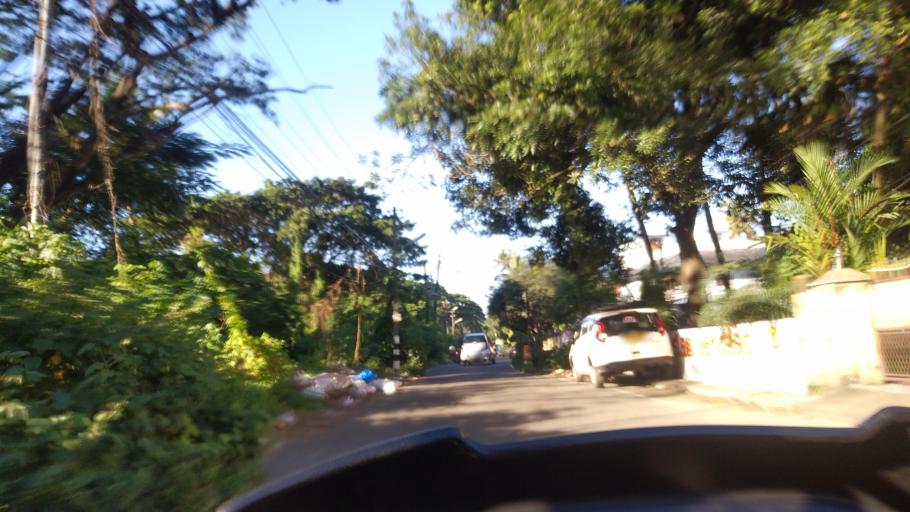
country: IN
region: Kerala
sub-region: Ernakulam
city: Cochin
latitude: 9.9978
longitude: 76.2783
